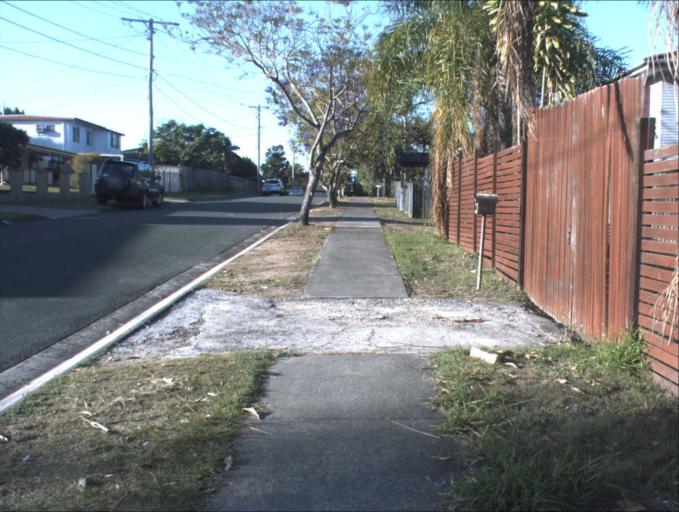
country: AU
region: Queensland
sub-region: Logan
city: Logan City
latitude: -27.6493
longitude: 153.1075
